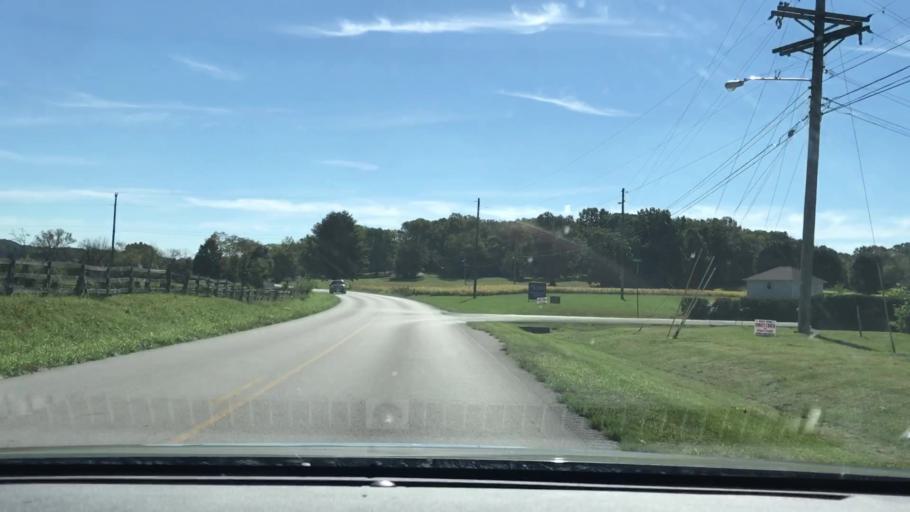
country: US
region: Kentucky
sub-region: Logan County
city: Russellville
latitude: 36.8334
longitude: -86.8682
